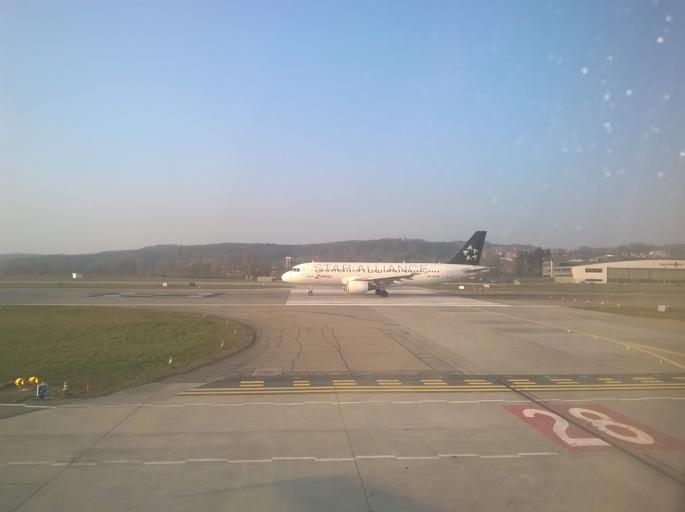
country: CH
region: Zurich
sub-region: Bezirk Buelach
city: Kloten / Holberg
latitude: 47.4557
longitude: 8.5699
